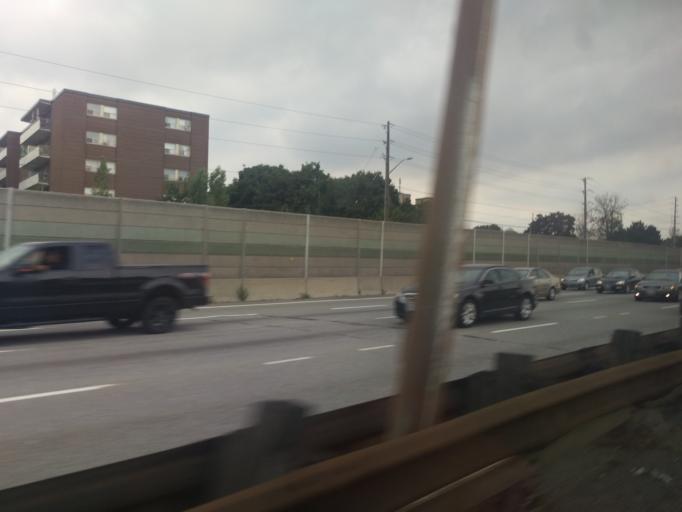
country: CA
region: Ontario
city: Mississauga
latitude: 43.5798
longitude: -79.5872
